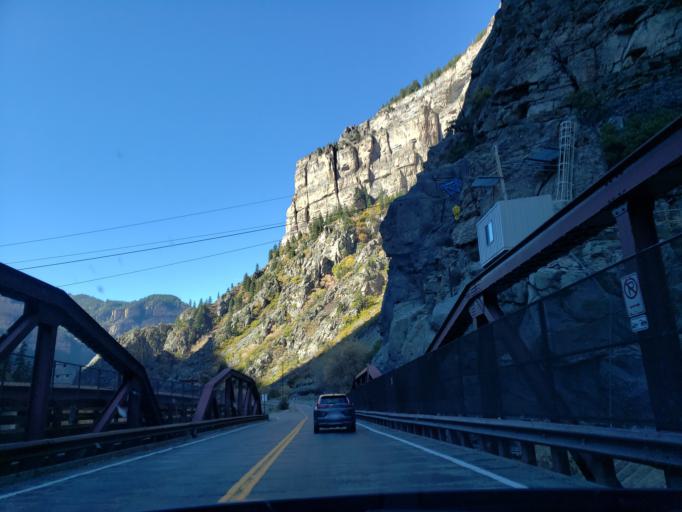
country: US
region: Colorado
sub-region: Garfield County
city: Glenwood Springs
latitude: 39.5881
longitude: -107.1938
